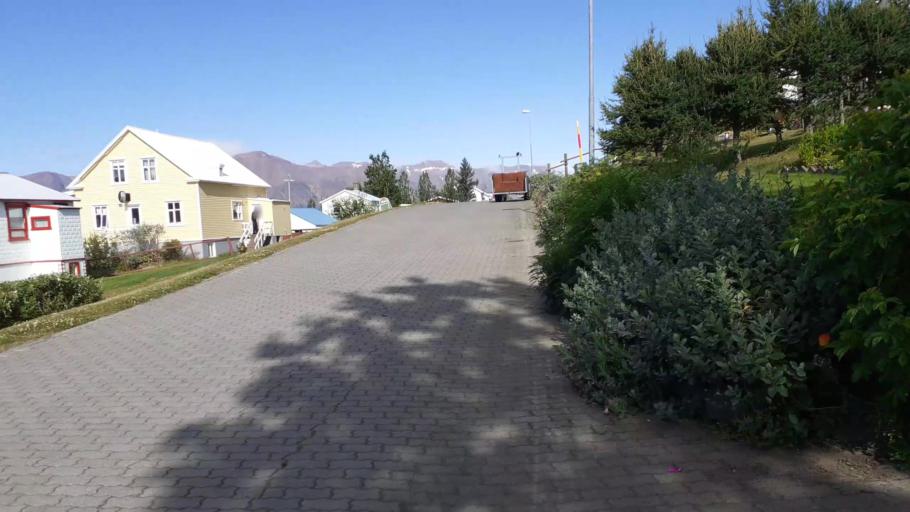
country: IS
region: Northeast
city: Dalvik
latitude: 65.9797
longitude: -18.3754
